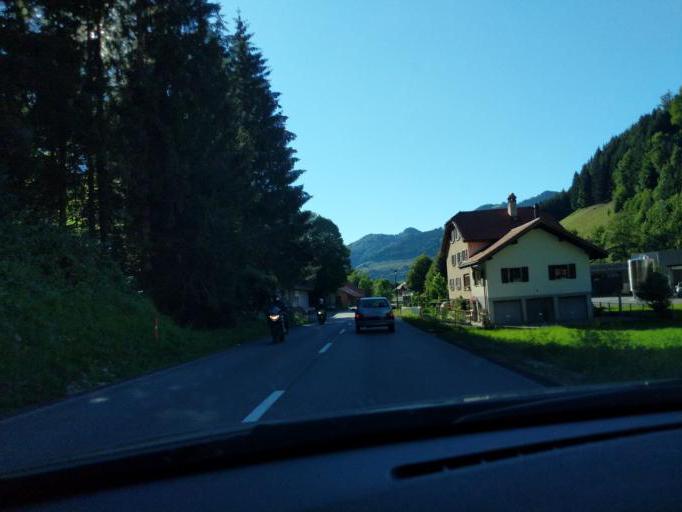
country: CH
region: Fribourg
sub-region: Gruyere District
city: Charmey
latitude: 46.6117
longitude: 7.1754
